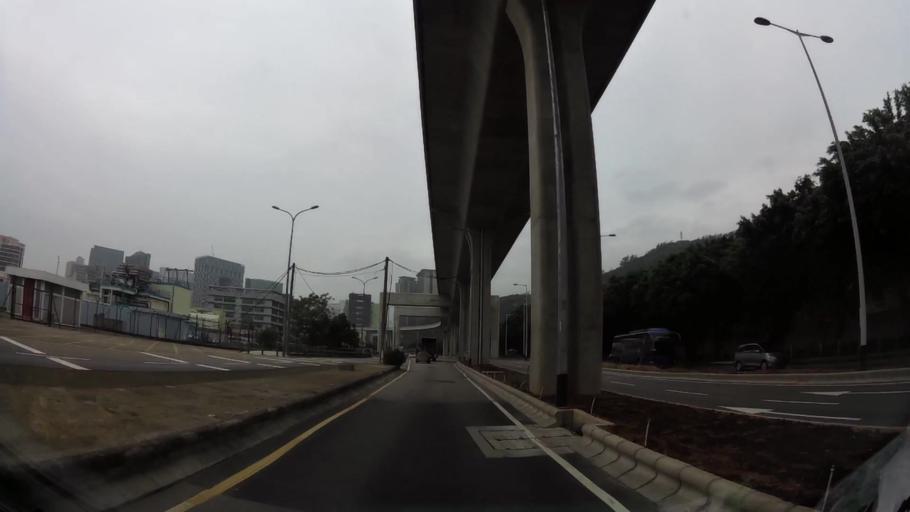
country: MO
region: Macau
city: Macau
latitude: 22.1567
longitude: 113.5718
